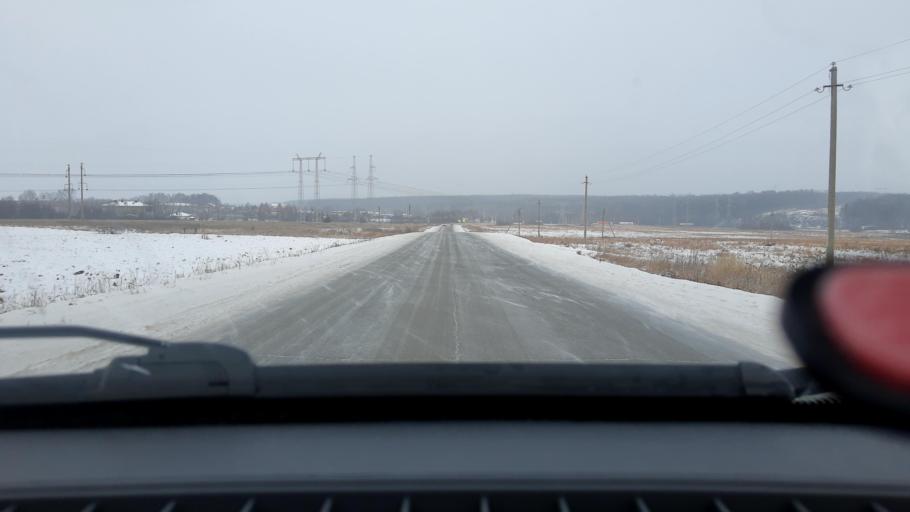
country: RU
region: Bashkortostan
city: Iglino
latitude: 54.7549
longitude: 56.3988
